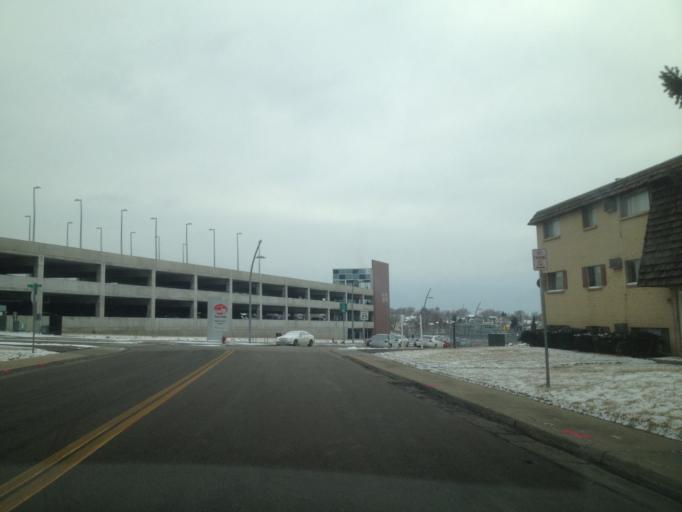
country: US
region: Colorado
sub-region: Adams County
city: Westminster
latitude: 39.8246
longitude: -105.0280
